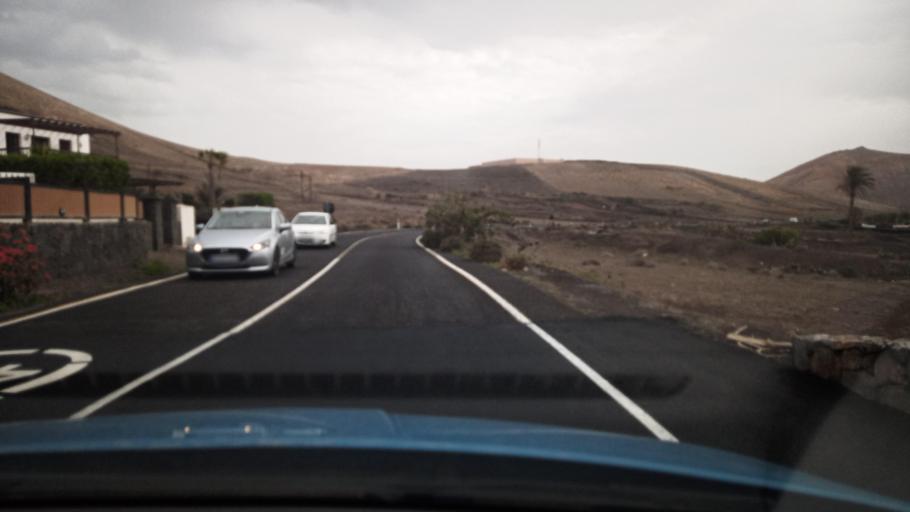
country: ES
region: Canary Islands
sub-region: Provincia de Las Palmas
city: Yaiza
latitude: 28.9471
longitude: -13.7394
